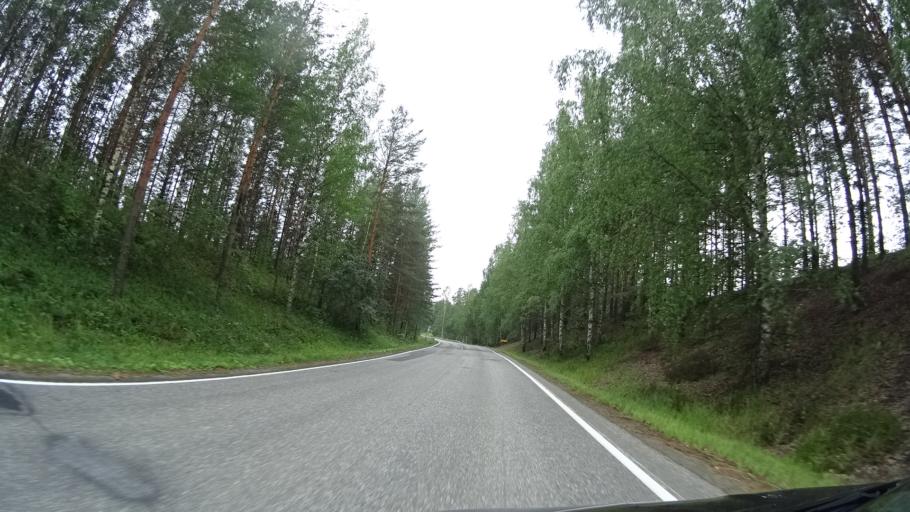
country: FI
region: Southern Savonia
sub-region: Savonlinna
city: Punkaharju
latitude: 61.7581
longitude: 29.4011
